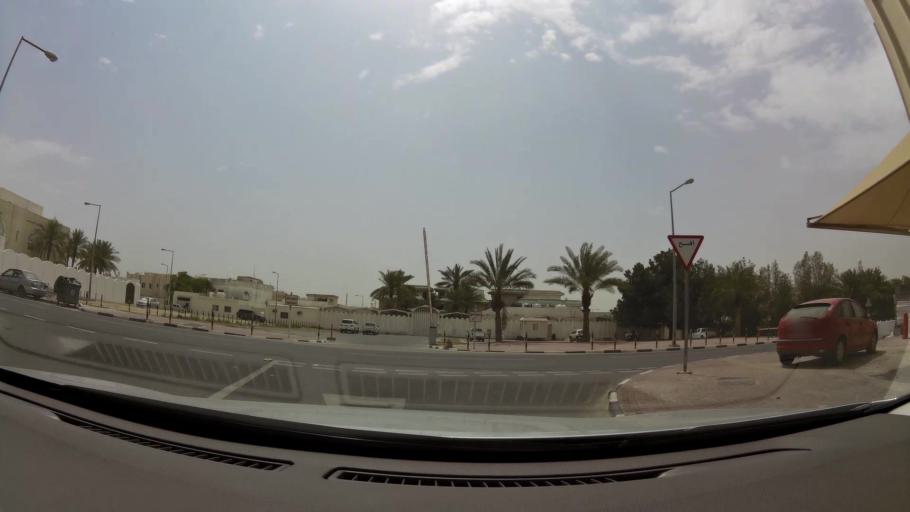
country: QA
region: Baladiyat ar Rayyan
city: Ar Rayyan
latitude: 25.3161
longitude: 51.4770
